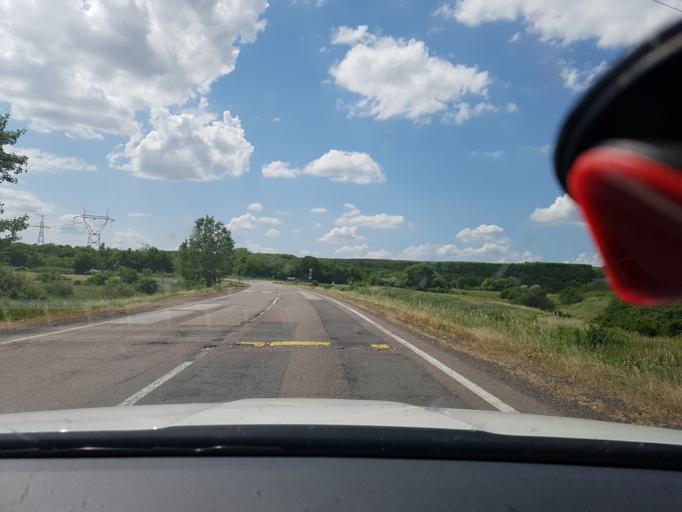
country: HU
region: Heves
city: Karacsond
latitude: 47.7413
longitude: 20.0902
